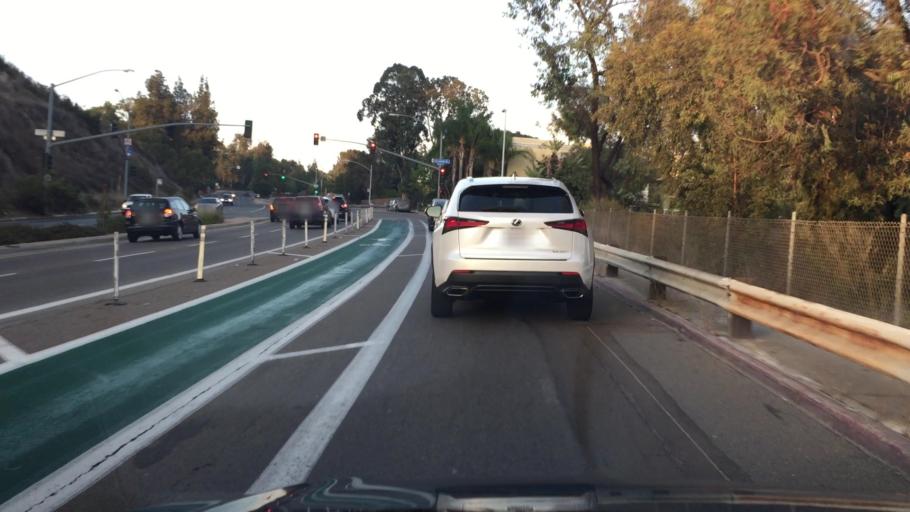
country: US
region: California
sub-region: San Diego County
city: Lemon Grove
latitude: 32.7697
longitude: -117.0868
